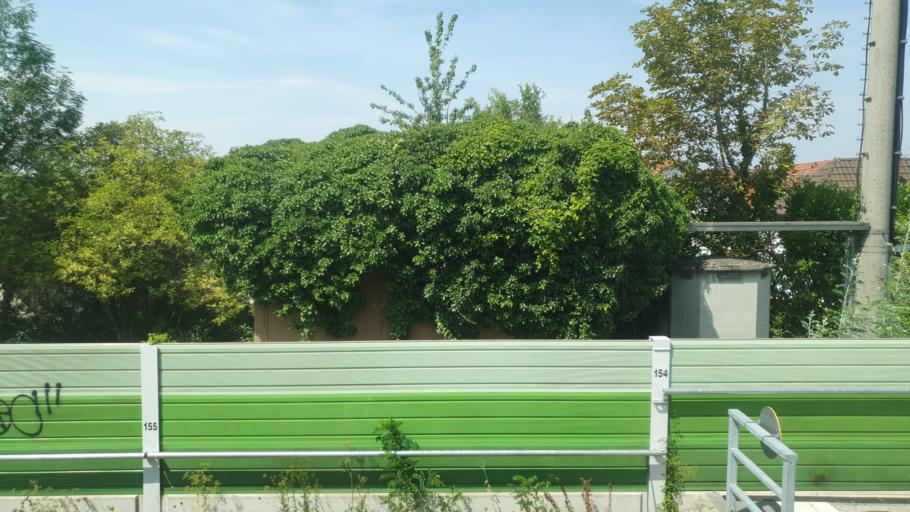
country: DE
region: Baden-Wuerttemberg
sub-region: Freiburg Region
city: Bad Bellingen
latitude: 47.7297
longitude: 7.5572
